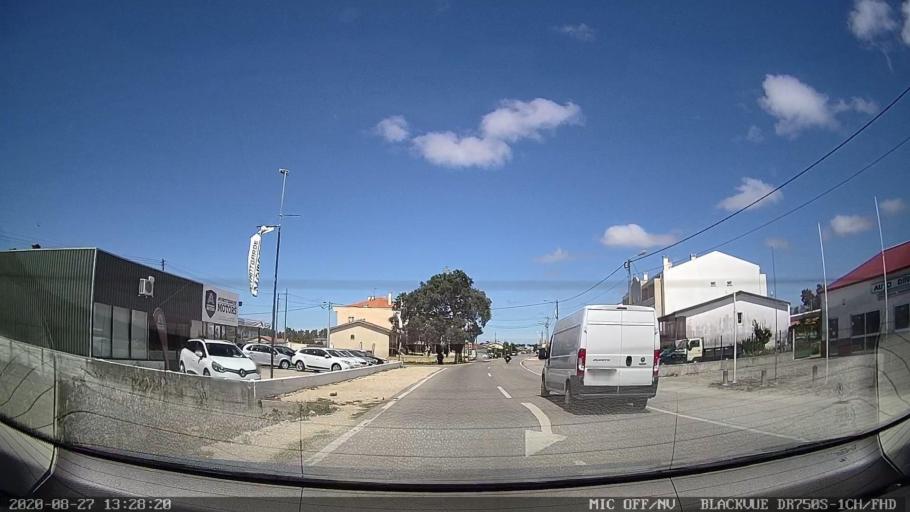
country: PT
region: Aveiro
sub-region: Vagos
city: Vagos
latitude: 40.5214
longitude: -8.6793
